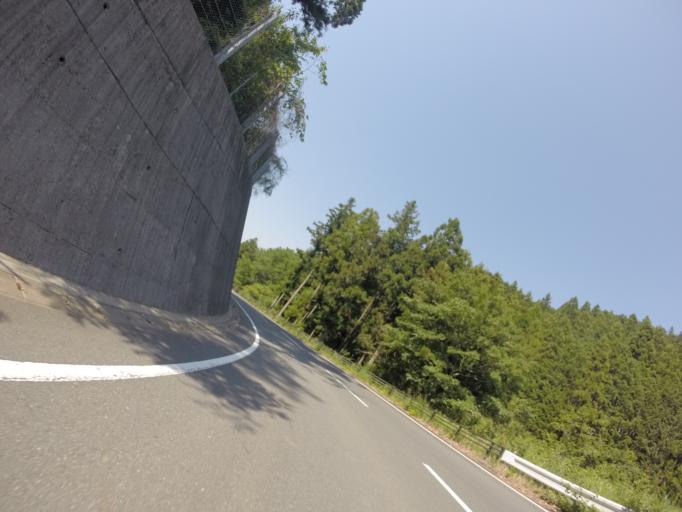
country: JP
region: Shizuoka
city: Fujinomiya
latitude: 35.1688
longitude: 138.5763
